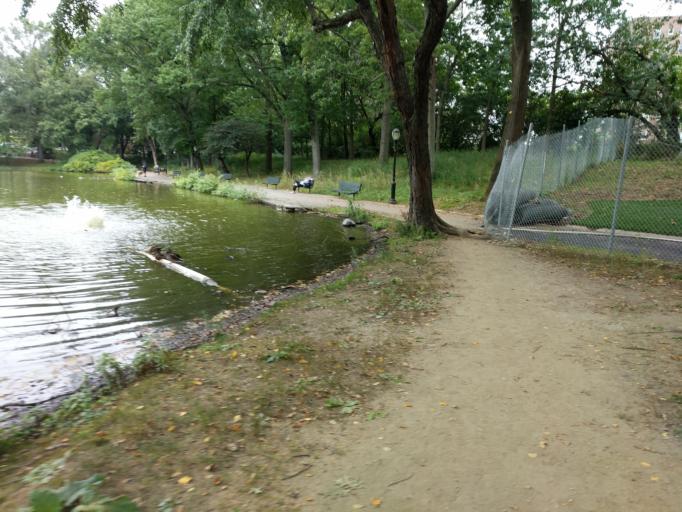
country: US
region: New York
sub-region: Queens County
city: Jamaica
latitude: 40.7116
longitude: -73.7985
